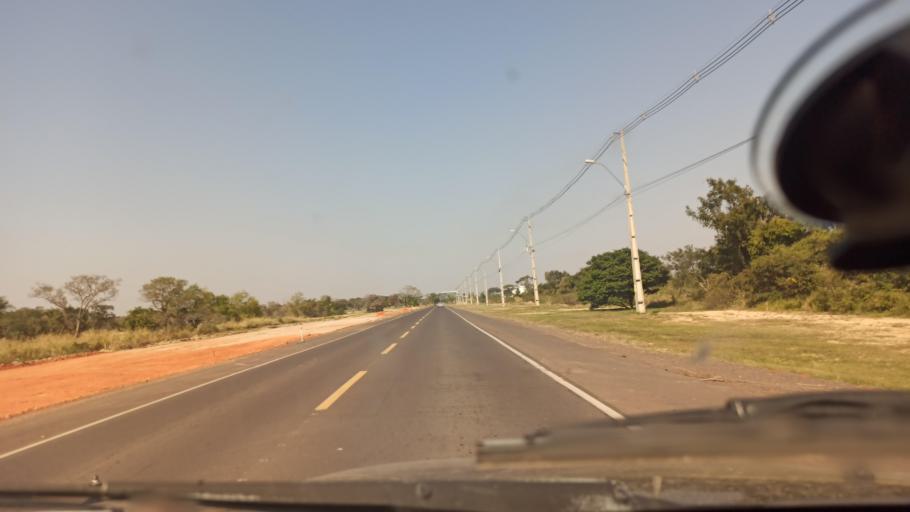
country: PY
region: Central
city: Colonia Mariano Roque Alonso
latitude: -25.1920
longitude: -57.5764
